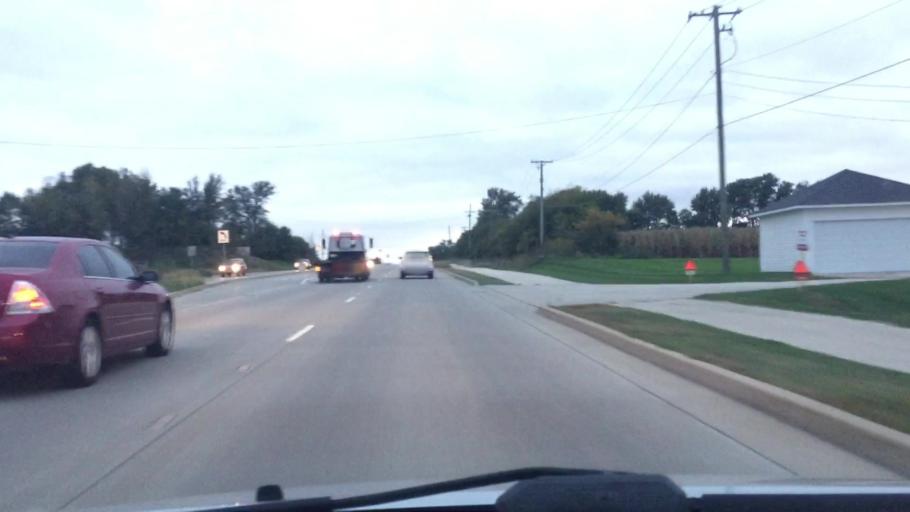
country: US
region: Illinois
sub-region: McHenry County
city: Algonquin
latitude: 42.1987
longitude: -88.2864
